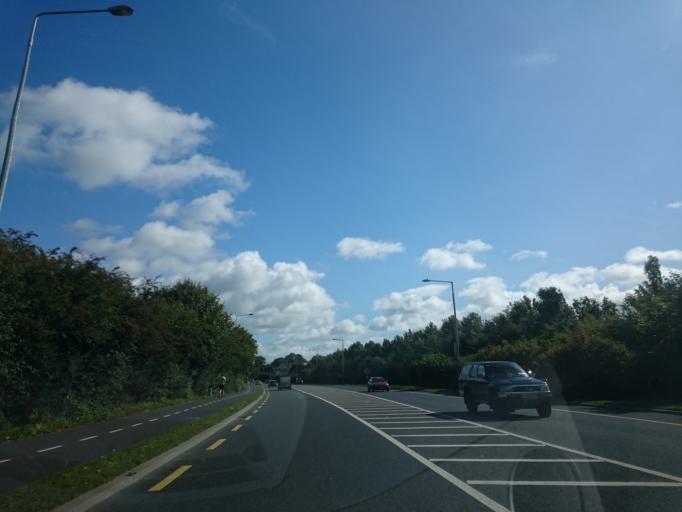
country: IE
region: Leinster
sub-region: Kilkenny
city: Kilkenny
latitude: 52.6363
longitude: -7.2412
